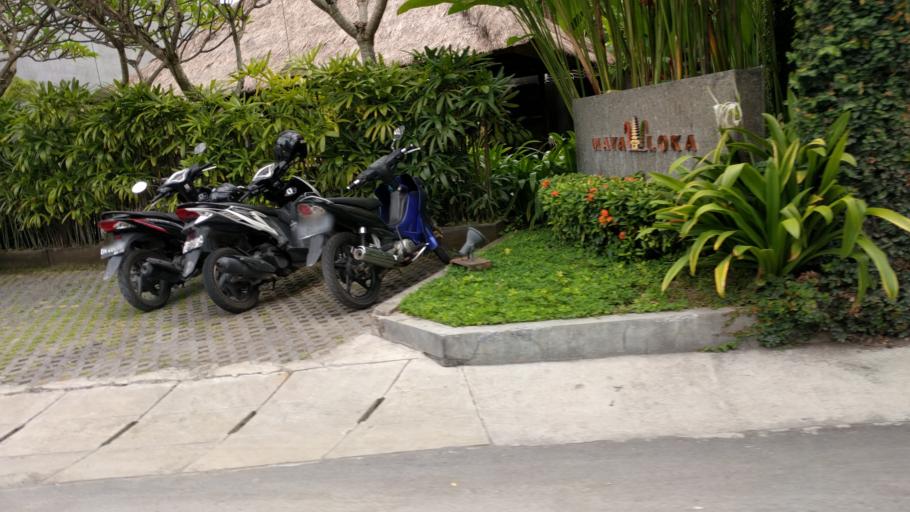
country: ID
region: Bali
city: Kuta
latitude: -8.6748
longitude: 115.1533
